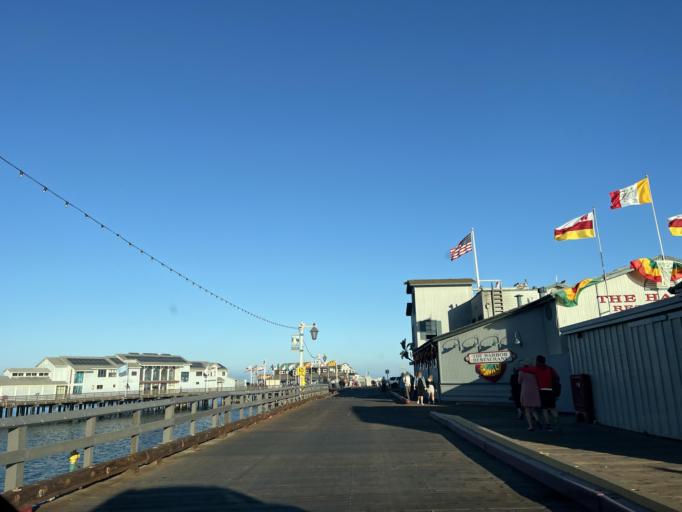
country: US
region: California
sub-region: Santa Barbara County
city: Santa Barbara
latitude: 34.4109
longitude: -119.6871
